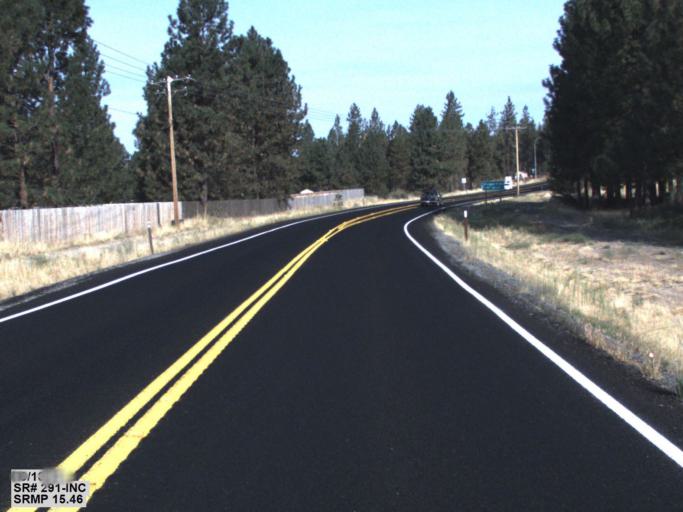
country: US
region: Washington
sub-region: Spokane County
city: Deer Park
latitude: 47.8324
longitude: -117.6021
